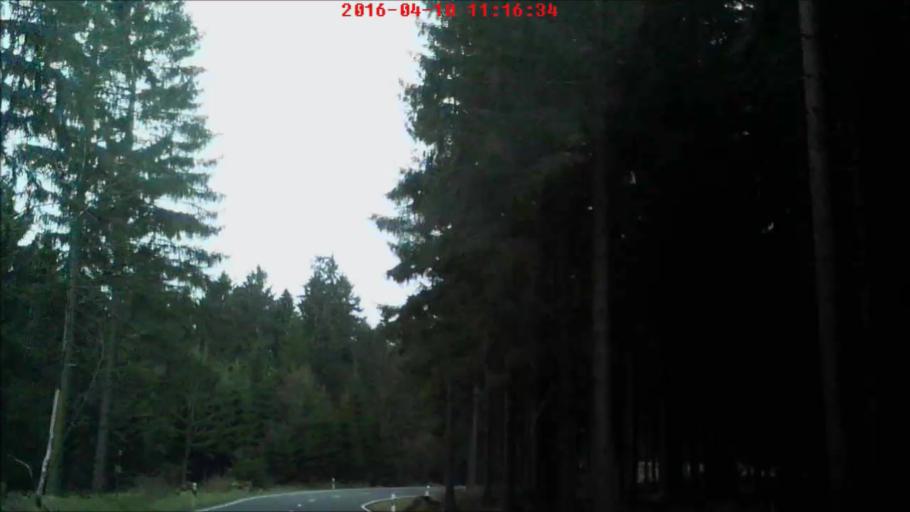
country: DE
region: Thuringia
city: Schmiedefeld am Rennsteig
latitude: 50.6077
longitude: 10.8422
